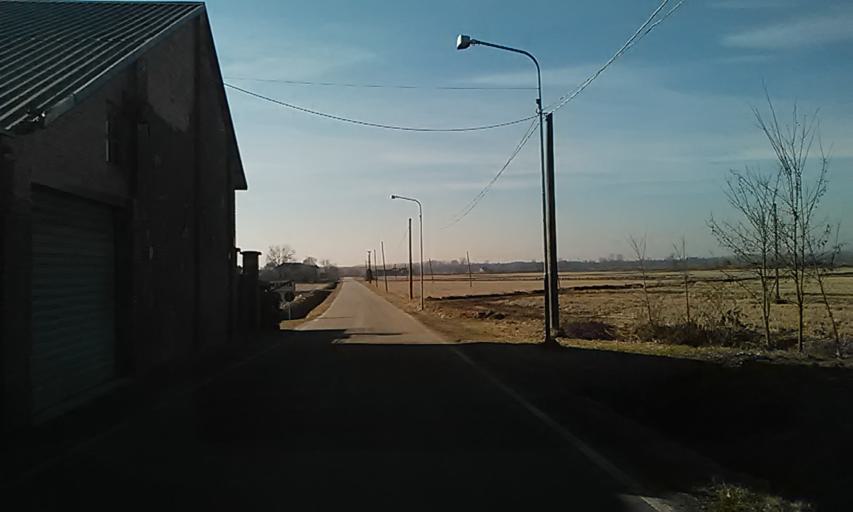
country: IT
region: Piedmont
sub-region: Provincia di Vercelli
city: Balocco
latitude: 45.4651
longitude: 8.2850
